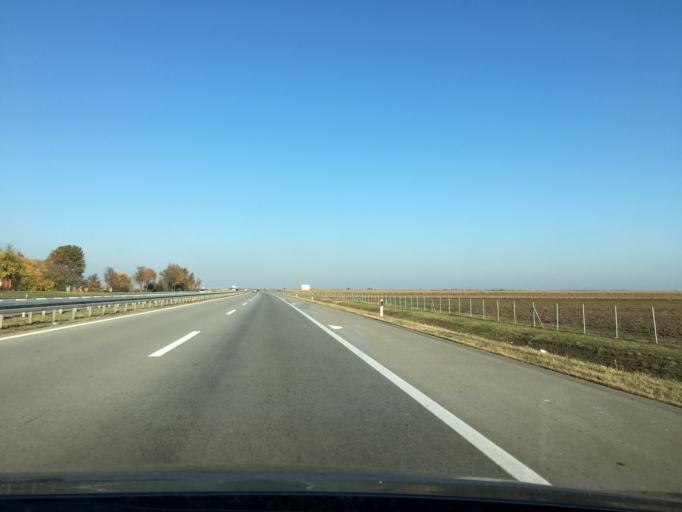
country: RS
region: Autonomna Pokrajina Vojvodina
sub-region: Juznobacki Okrug
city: Kovilj
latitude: 45.2161
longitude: 20.0641
